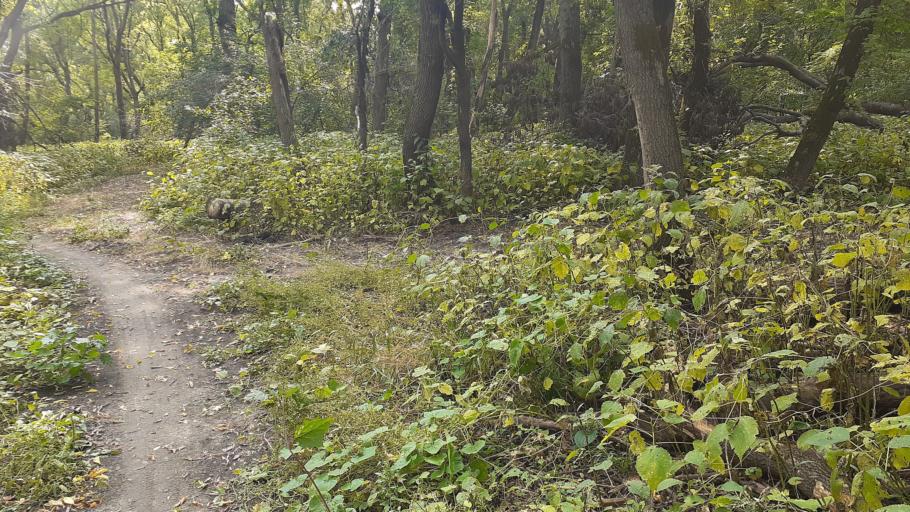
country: US
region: Minnesota
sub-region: Clay County
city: Oakport
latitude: 46.9108
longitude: -96.7599
